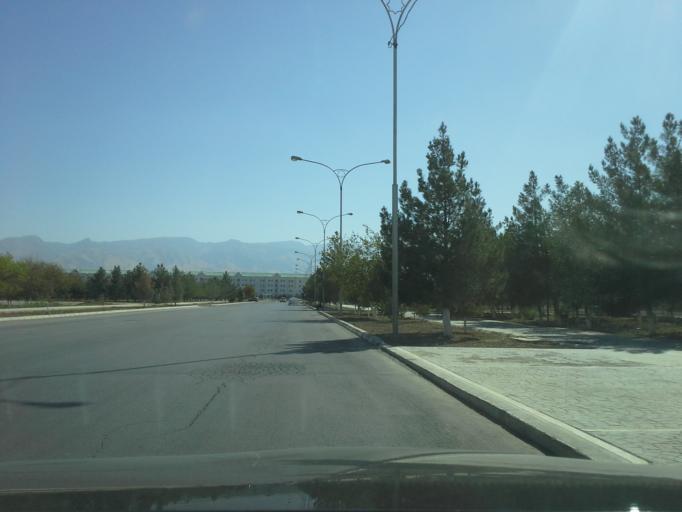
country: TM
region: Ahal
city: Ashgabat
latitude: 37.9936
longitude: 58.3226
